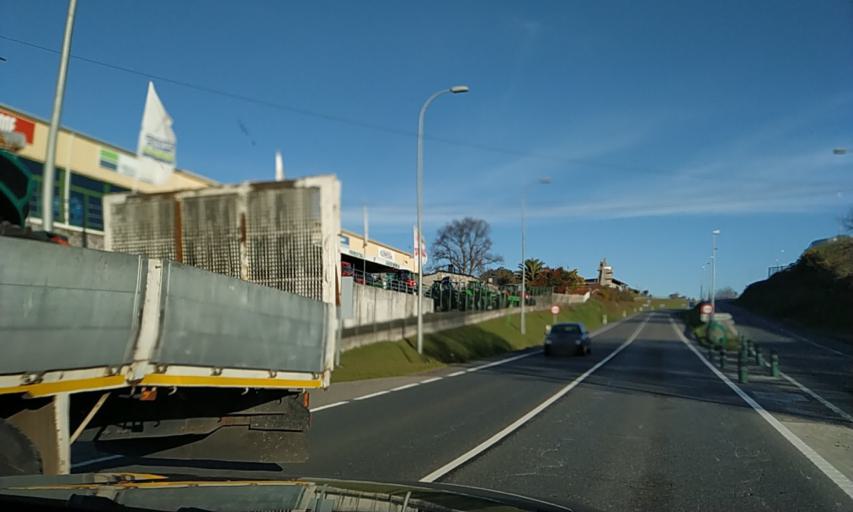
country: ES
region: Galicia
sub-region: Provincia de Pontevedra
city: Silleda
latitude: 42.6942
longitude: -8.2300
